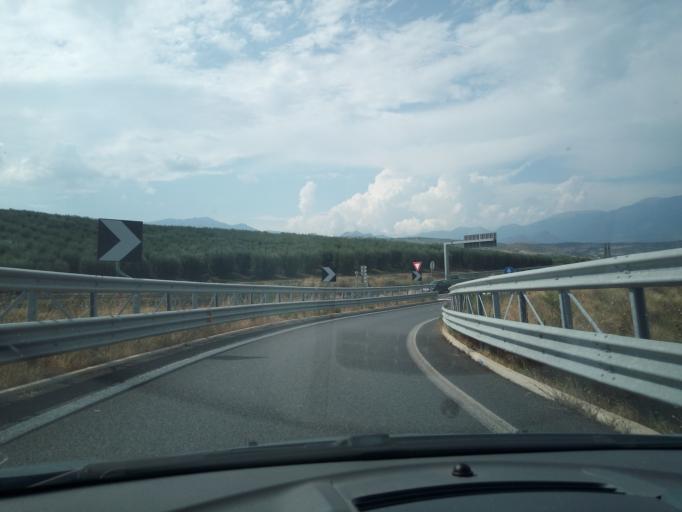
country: IT
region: Calabria
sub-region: Provincia di Cosenza
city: Firmo
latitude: 39.7214
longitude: 16.2370
